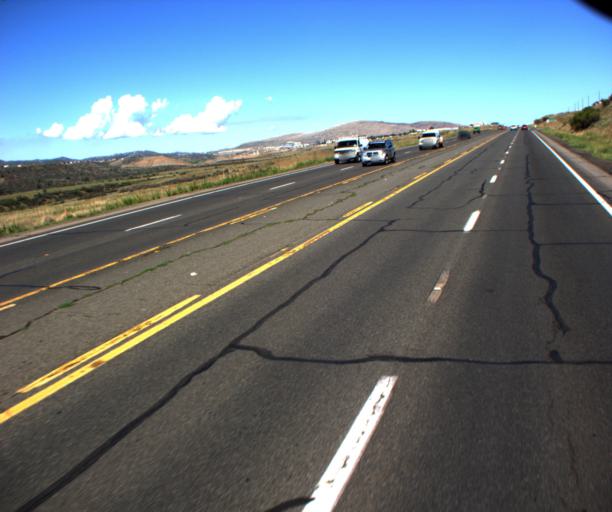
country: US
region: Arizona
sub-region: Yavapai County
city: Prescott Valley
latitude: 34.5796
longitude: -112.2981
